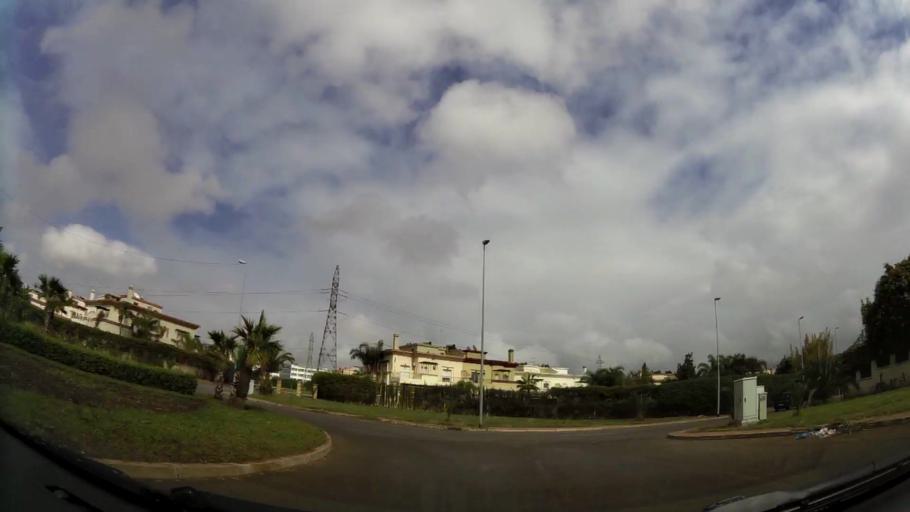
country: MA
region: Grand Casablanca
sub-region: Casablanca
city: Casablanca
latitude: 33.5294
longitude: -7.6195
